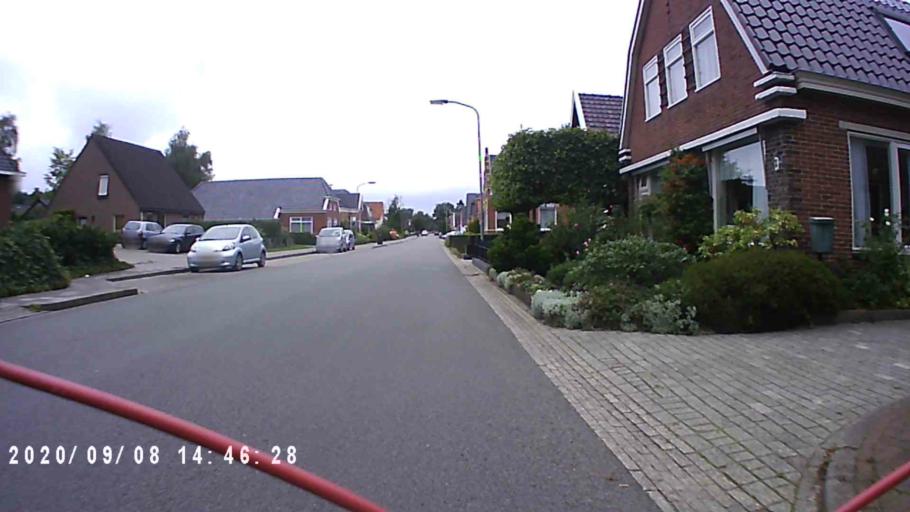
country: NL
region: Groningen
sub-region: Gemeente Slochteren
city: Slochteren
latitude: 53.2338
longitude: 6.8153
